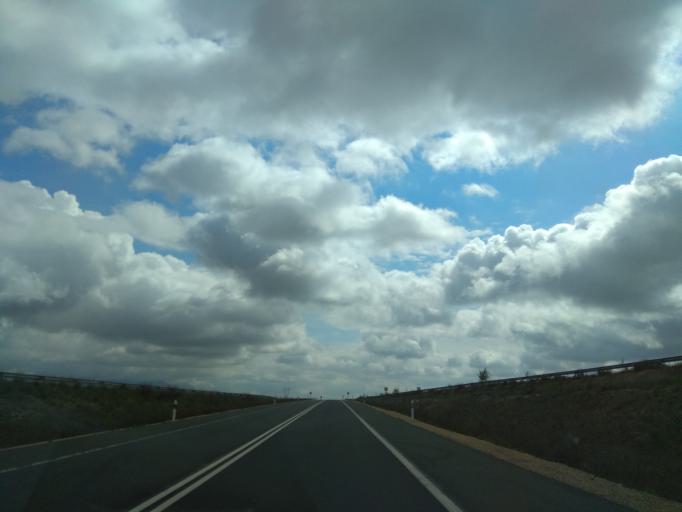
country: ES
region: La Rioja
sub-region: Provincia de La Rioja
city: Zarraton
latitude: 42.5437
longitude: -2.8780
